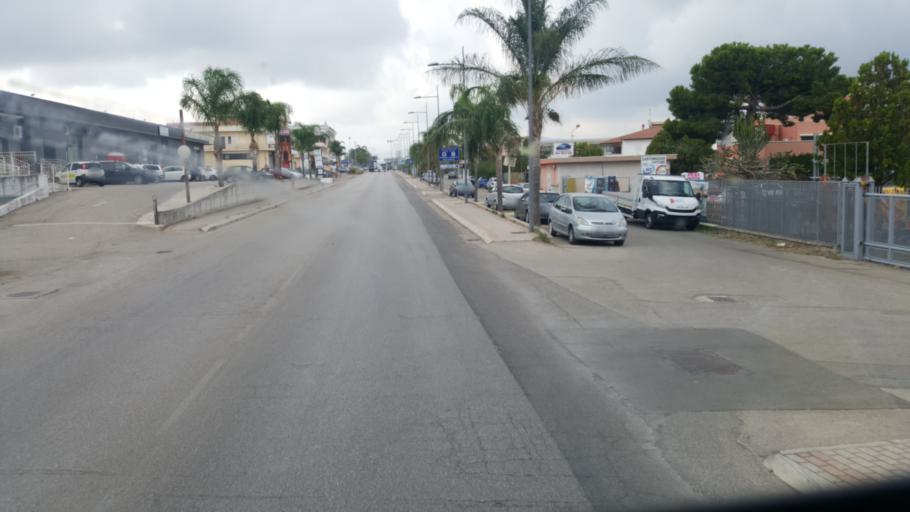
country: IT
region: Campania
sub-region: Provincia di Salerno
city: Battipaglia
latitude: 40.5976
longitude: 14.9881
